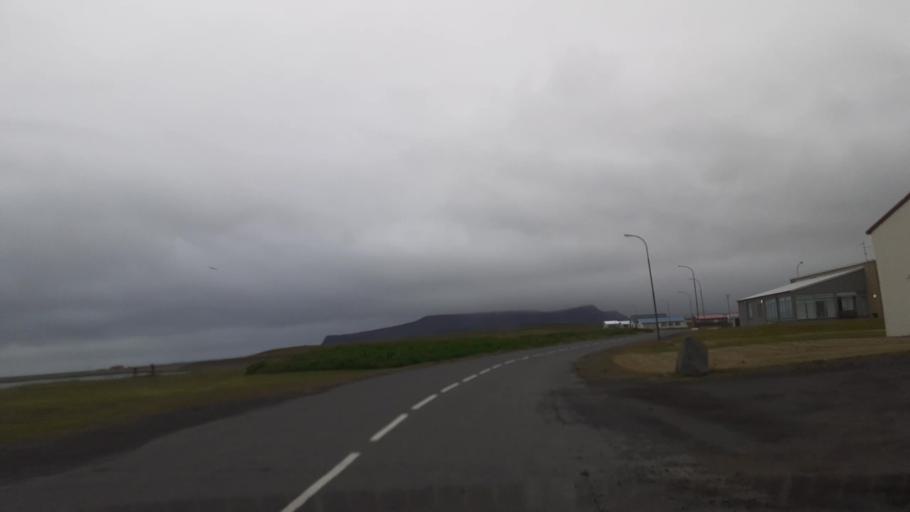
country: IS
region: Northeast
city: Husavik
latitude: 66.3004
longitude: -16.4488
